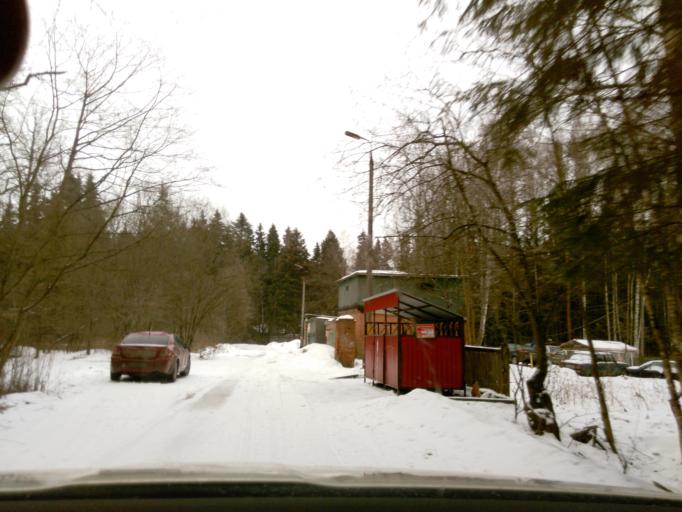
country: RU
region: Moskovskaya
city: Skhodnya
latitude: 55.9691
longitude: 37.2812
